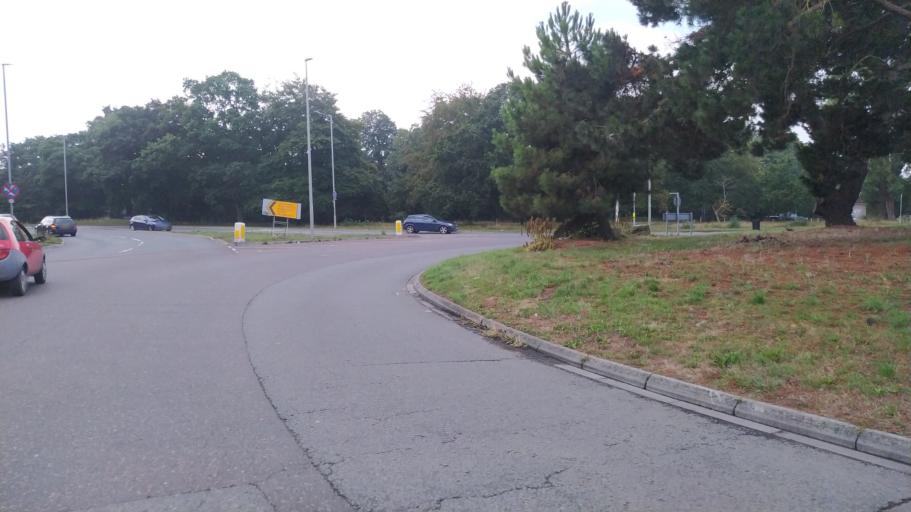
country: GB
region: England
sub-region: Hampshire
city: Bransgore
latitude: 50.7430
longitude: -1.7406
